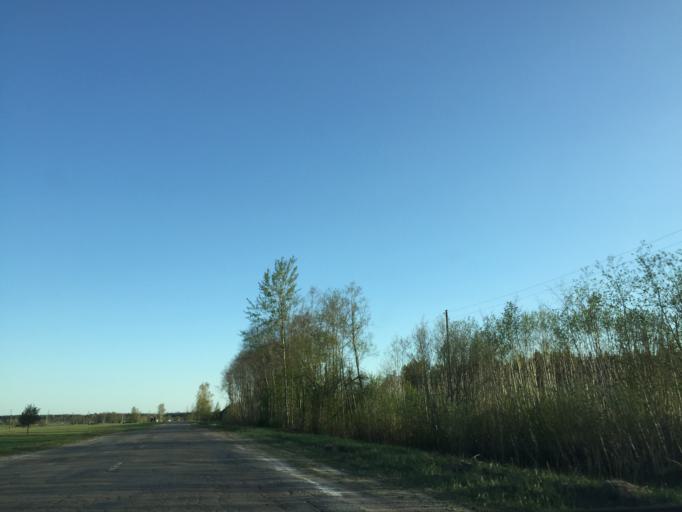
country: LV
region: Koknese
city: Koknese
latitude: 56.6908
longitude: 25.4870
